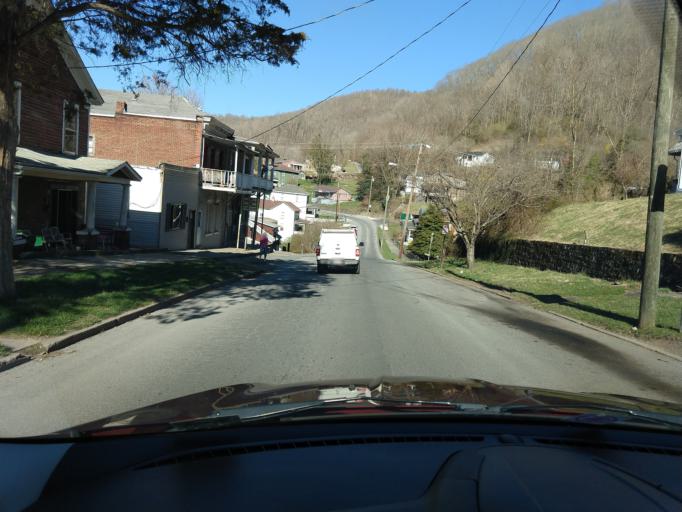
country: US
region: West Virginia
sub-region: Summers County
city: Hinton
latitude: 37.6789
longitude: -80.8788
